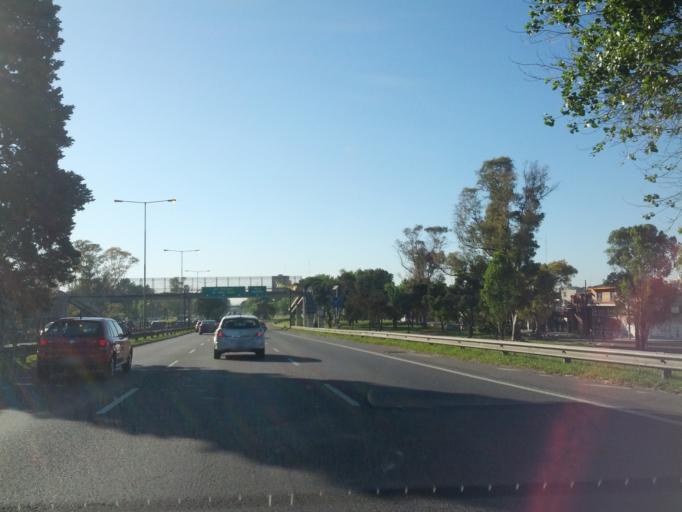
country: AR
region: Buenos Aires F.D.
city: Villa Lugano
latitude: -34.6778
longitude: -58.4975
